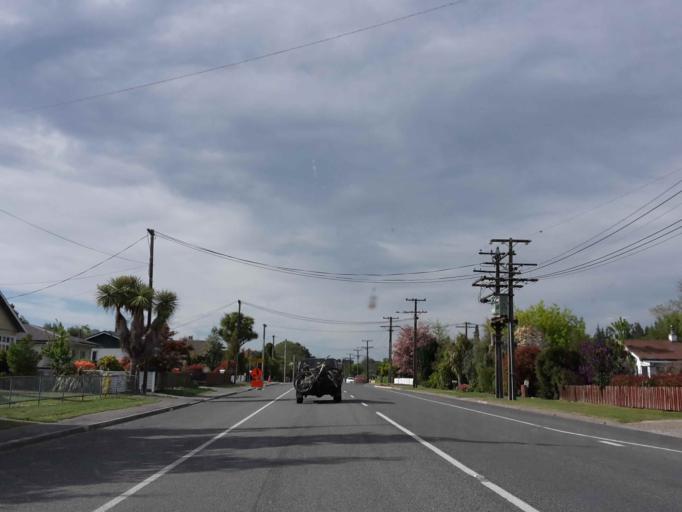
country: NZ
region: Canterbury
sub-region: Timaru District
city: Pleasant Point
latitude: -44.1016
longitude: 171.2381
